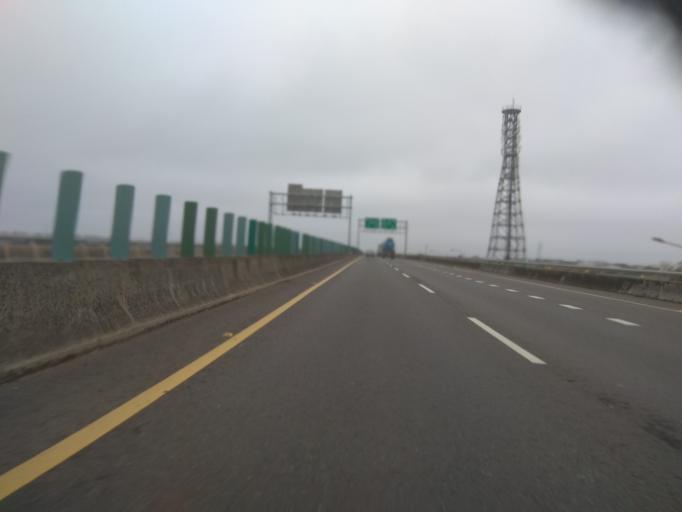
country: TW
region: Taiwan
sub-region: Hsinchu
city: Zhubei
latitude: 24.9977
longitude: 121.1043
